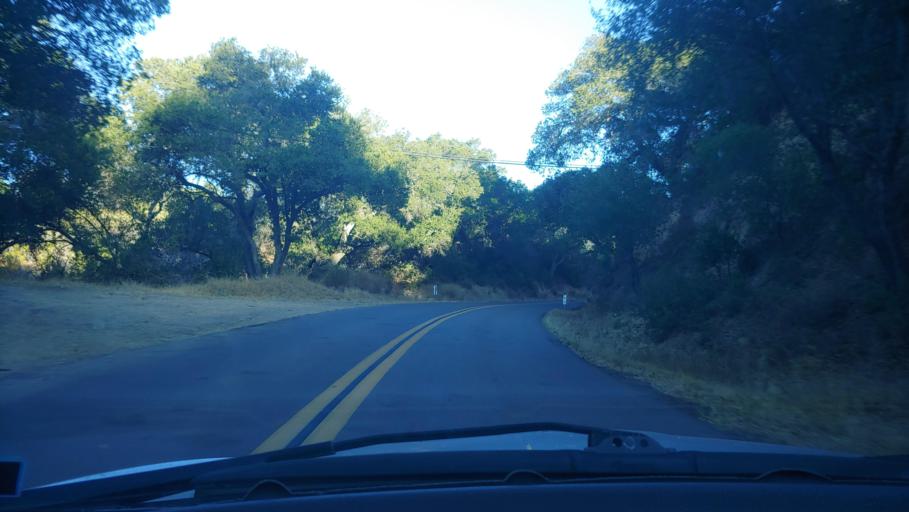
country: US
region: California
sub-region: Santa Barbara County
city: Goleta
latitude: 34.5322
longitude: -119.8394
